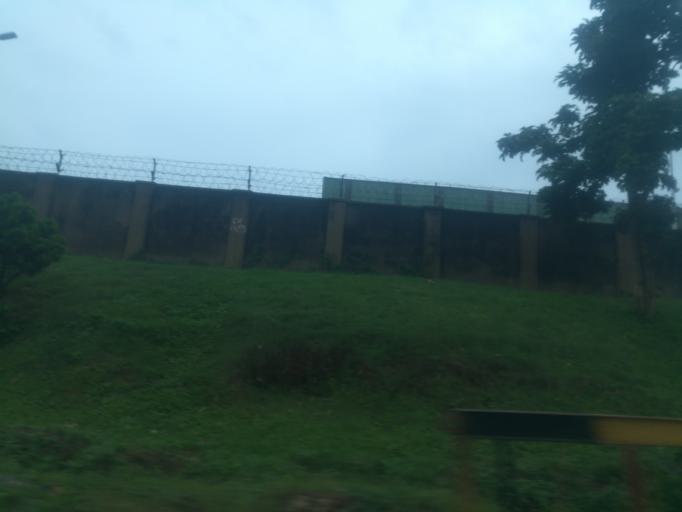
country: NG
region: Oyo
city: Ibadan
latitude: 7.4014
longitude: 3.9661
